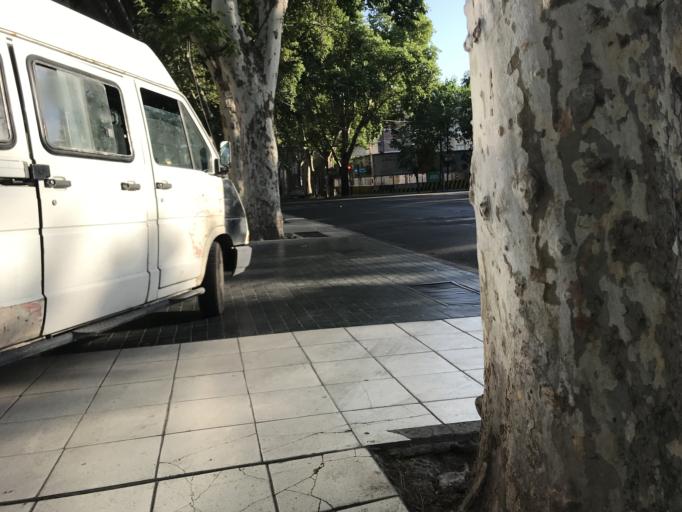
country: AR
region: Mendoza
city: Mendoza
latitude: -32.8888
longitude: -68.8457
